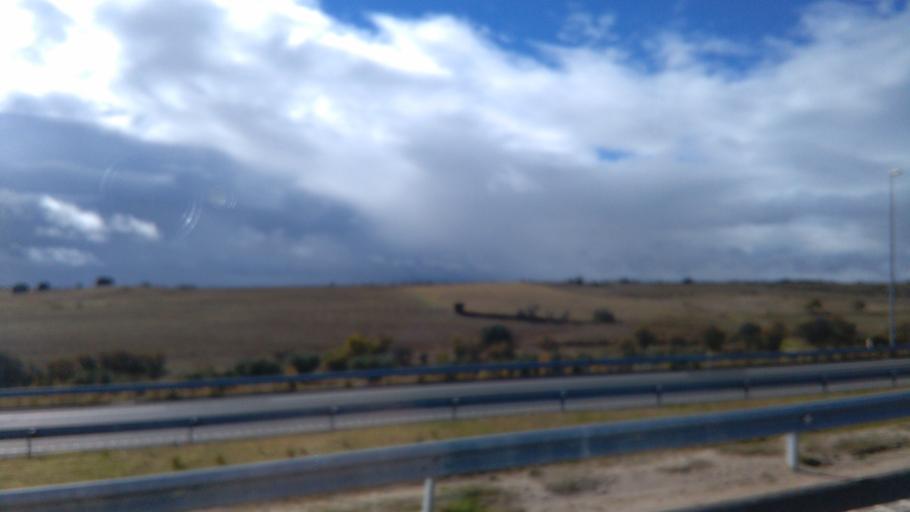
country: ES
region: Madrid
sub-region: Provincia de Madrid
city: Navalcarnero
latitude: 40.2664
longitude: -4.0304
